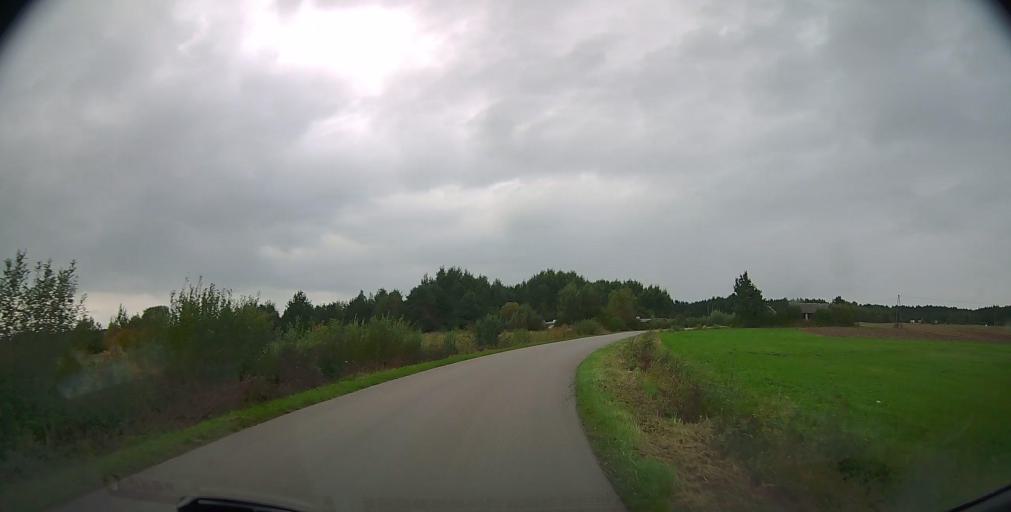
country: PL
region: Masovian Voivodeship
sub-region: Powiat radomski
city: Jedlinsk
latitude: 51.4558
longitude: 21.1036
